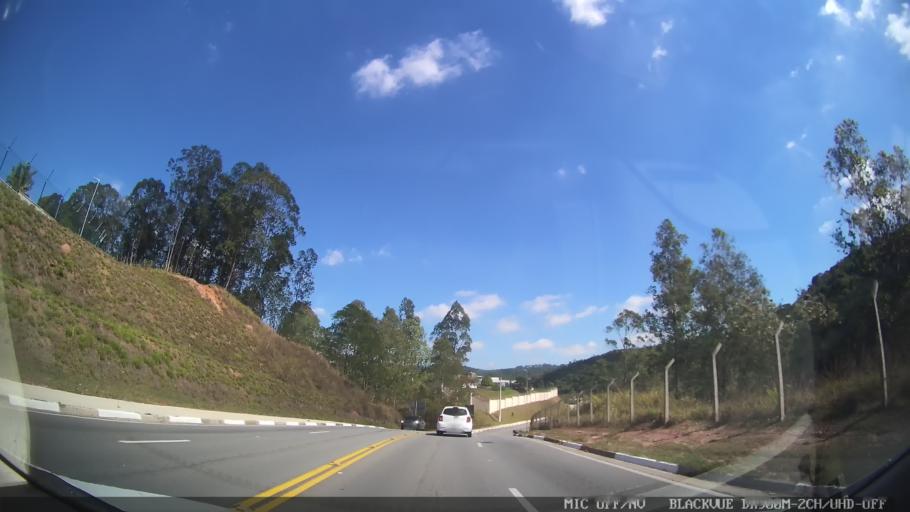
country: BR
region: Sao Paulo
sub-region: Santana De Parnaiba
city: Santana de Parnaiba
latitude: -23.4342
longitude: -46.8304
